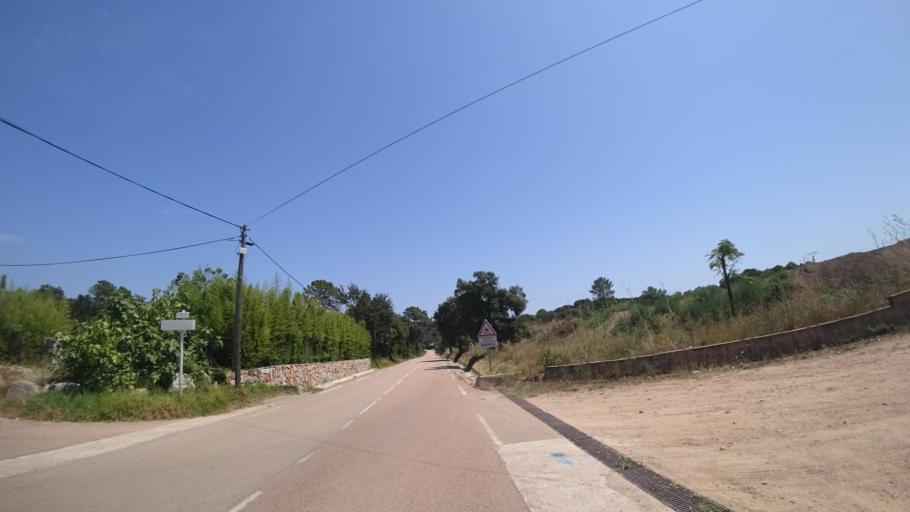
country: FR
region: Corsica
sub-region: Departement de la Corse-du-Sud
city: Porto-Vecchio
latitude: 41.6286
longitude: 9.2453
